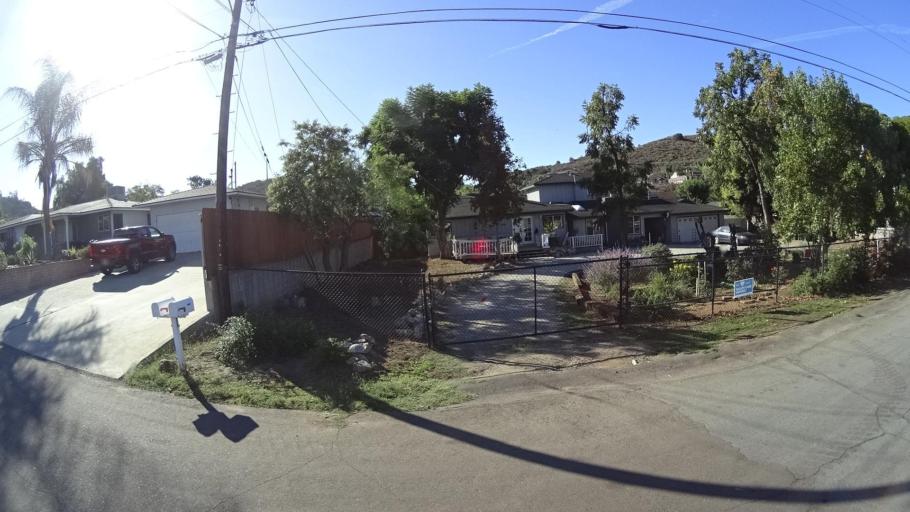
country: US
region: California
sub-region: San Diego County
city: Lakeside
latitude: 32.8559
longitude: -116.9046
